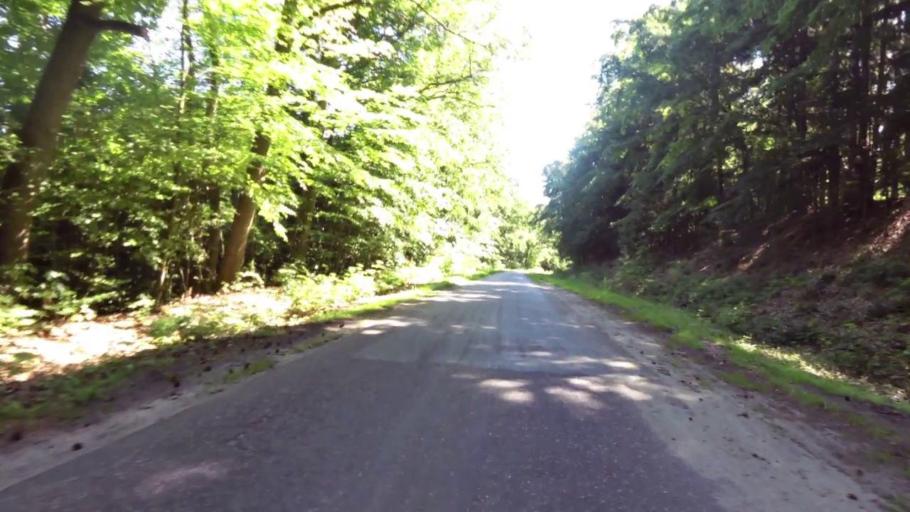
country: PL
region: West Pomeranian Voivodeship
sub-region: Powiat bialogardzki
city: Bialogard
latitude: 53.9416
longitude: 15.9634
